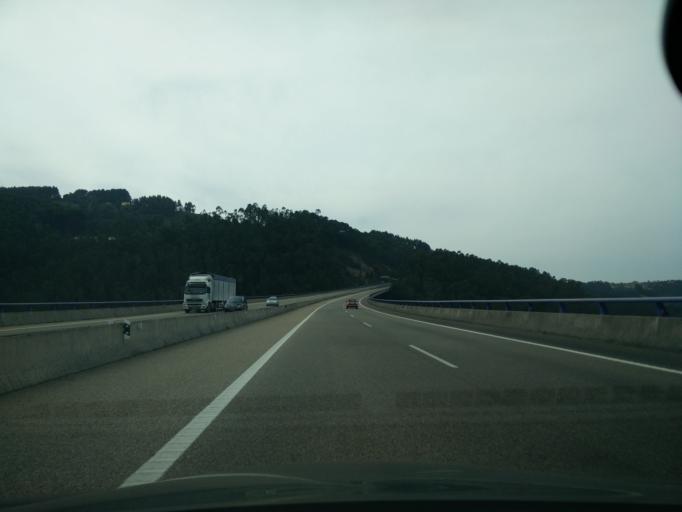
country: ES
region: Asturias
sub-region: Province of Asturias
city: Arriba
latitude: 43.4985
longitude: -5.5370
